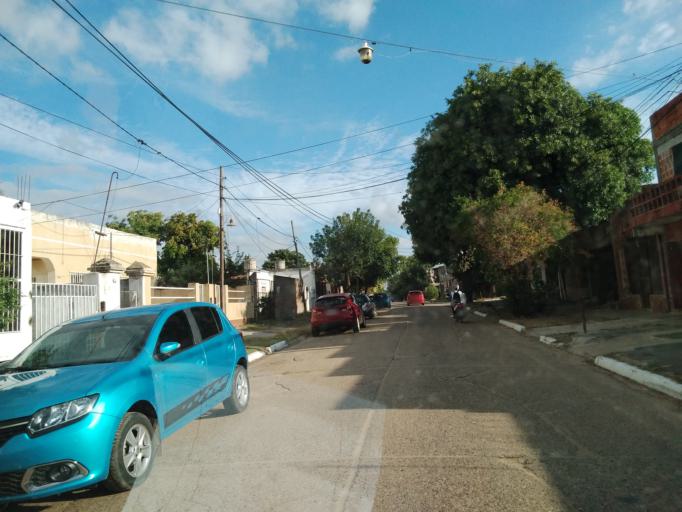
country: AR
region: Corrientes
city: Corrientes
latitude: -27.4603
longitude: -58.8192
